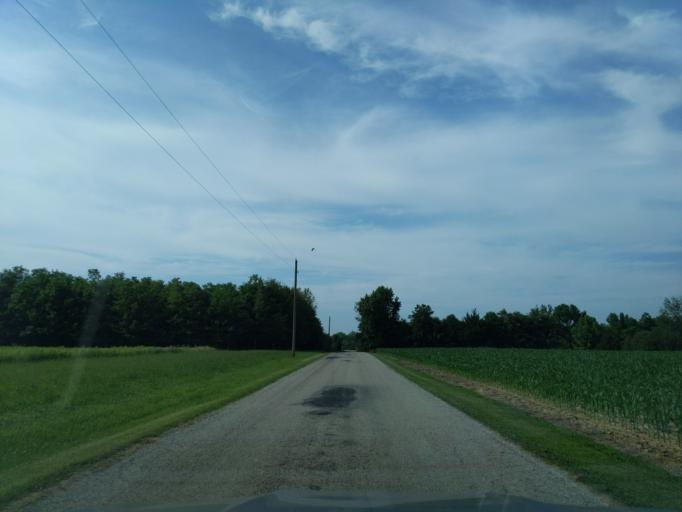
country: US
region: Indiana
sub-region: Ripley County
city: Osgood
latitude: 39.2078
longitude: -85.3893
